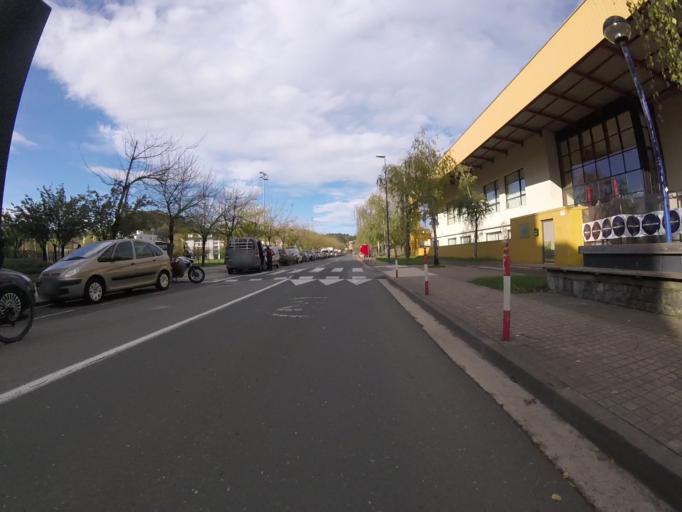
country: ES
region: Basque Country
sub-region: Provincia de Guipuzcoa
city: Hernani
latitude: 43.2719
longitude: -1.9721
